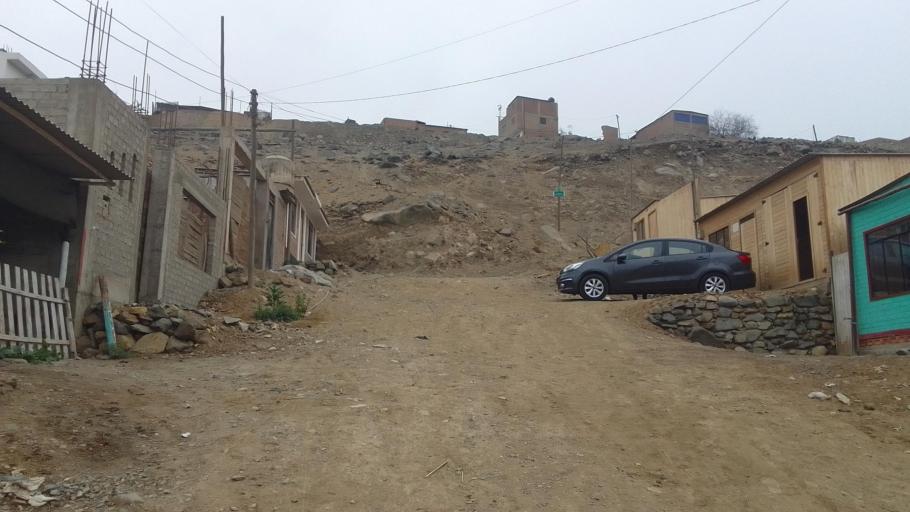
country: PE
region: Lima
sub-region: Lima
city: Santa Rosa
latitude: -11.8142
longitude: -77.1242
